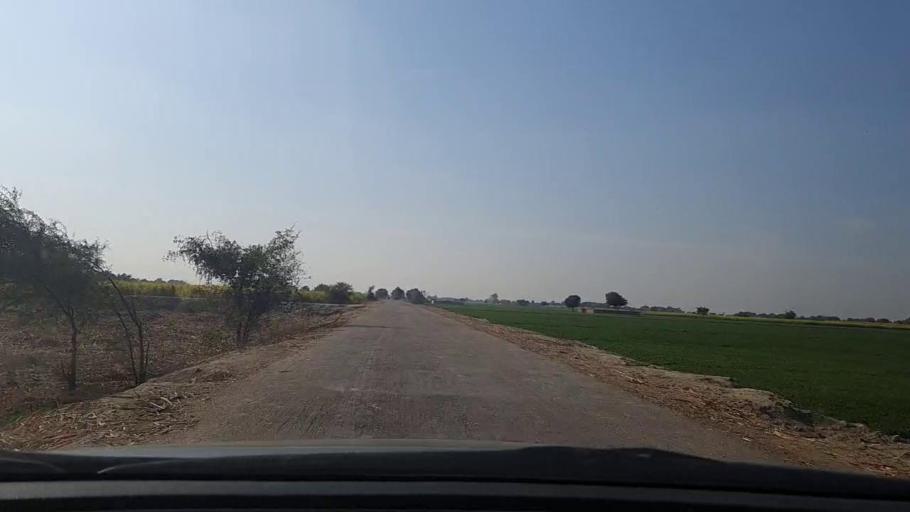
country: PK
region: Sindh
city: Daulatpur
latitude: 26.3204
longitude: 68.0369
